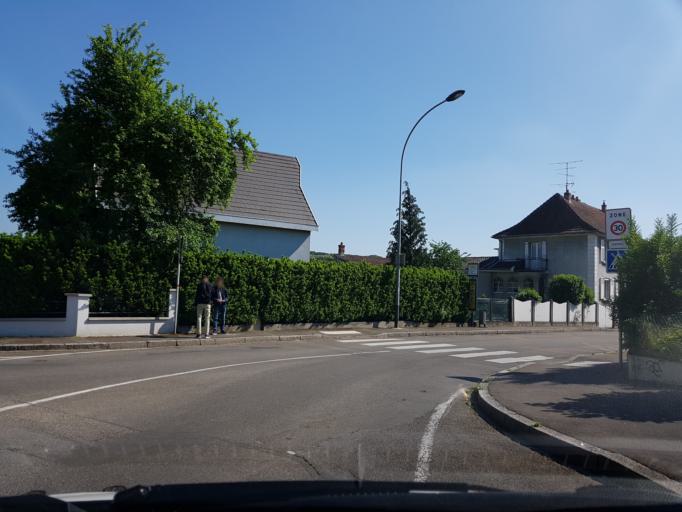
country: FR
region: Alsace
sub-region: Departement du Haut-Rhin
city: Riedisheim
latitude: 47.7403
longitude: 7.3659
